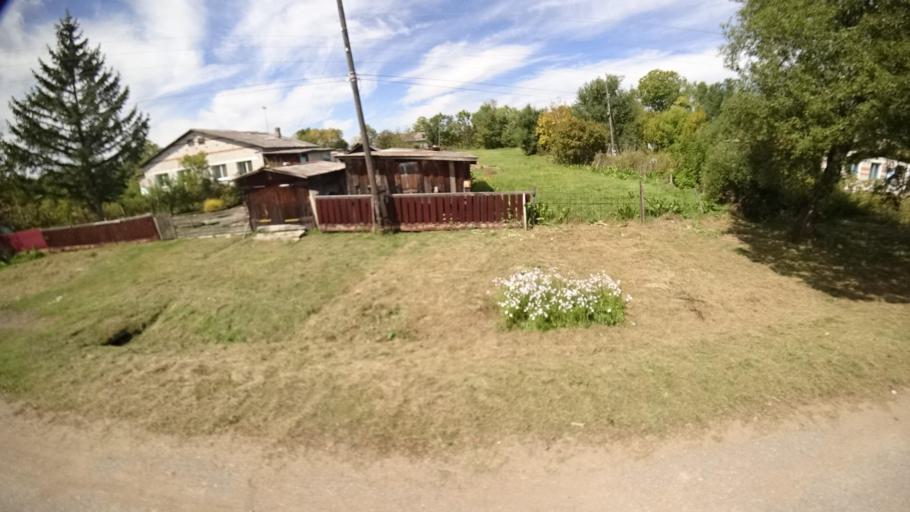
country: RU
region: Primorskiy
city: Yakovlevka
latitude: 44.6435
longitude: 133.5933
